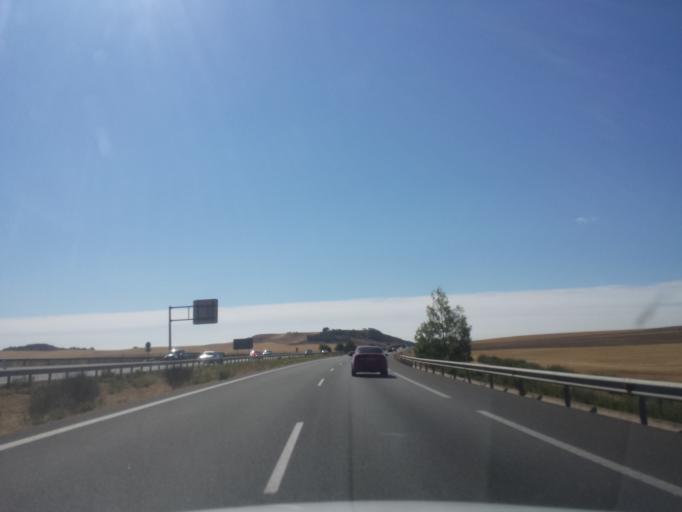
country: ES
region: Castille and Leon
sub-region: Provincia de Valladolid
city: Mota del Marques
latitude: 41.6231
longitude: -5.1652
